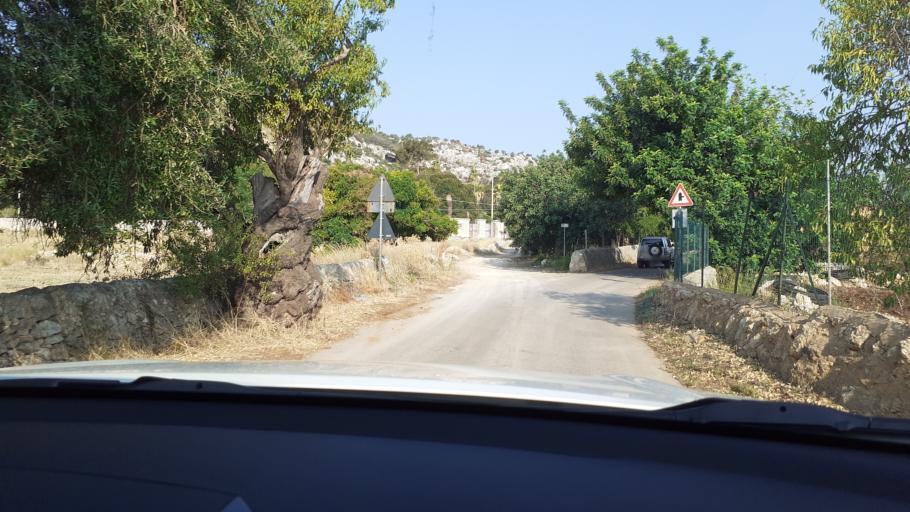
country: IT
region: Sicily
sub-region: Provincia di Siracusa
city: Cassibile
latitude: 36.9778
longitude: 15.1772
